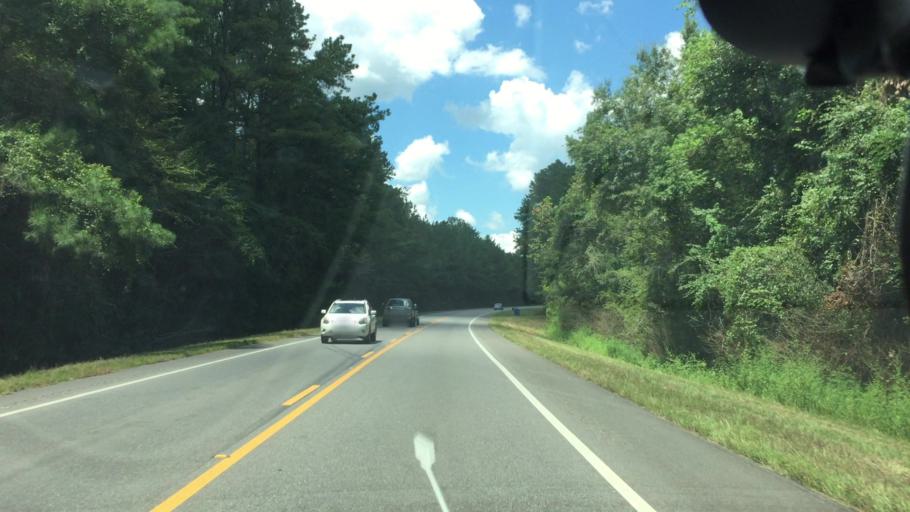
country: US
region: Alabama
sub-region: Pike County
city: Brundidge
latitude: 31.5939
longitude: -85.9446
